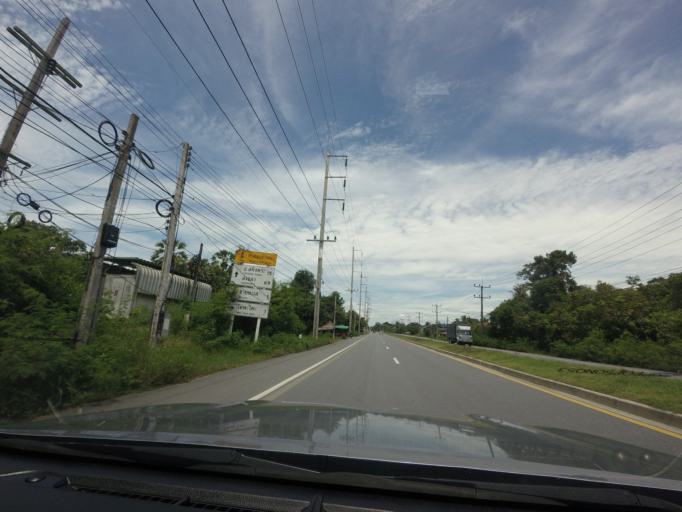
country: TH
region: Songkhla
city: Krasae Sin
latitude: 7.6080
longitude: 100.3993
